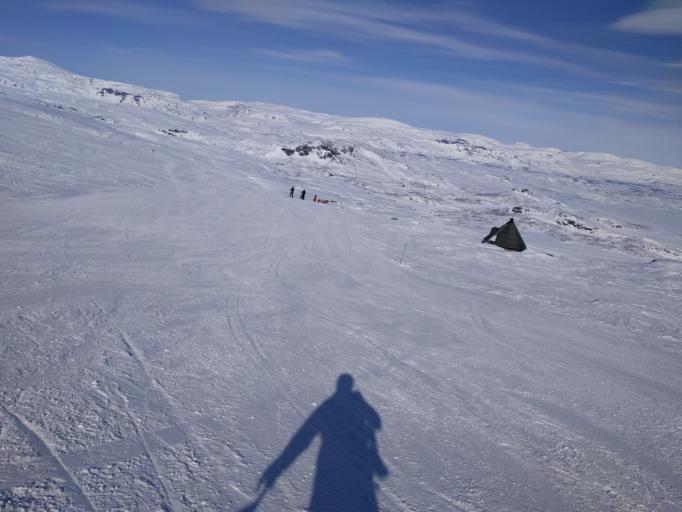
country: NO
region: Troms
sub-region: Lavangen
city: Tennevoll
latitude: 68.4205
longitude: 18.1033
